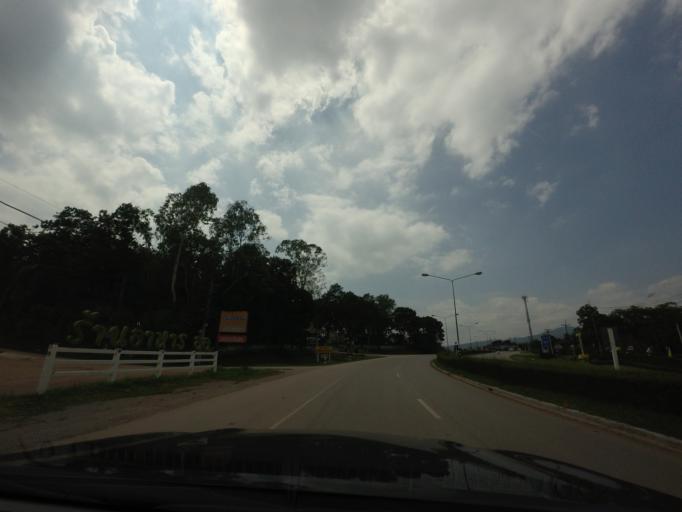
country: TH
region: Loei
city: Phu Ruea
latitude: 17.4491
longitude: 101.3549
